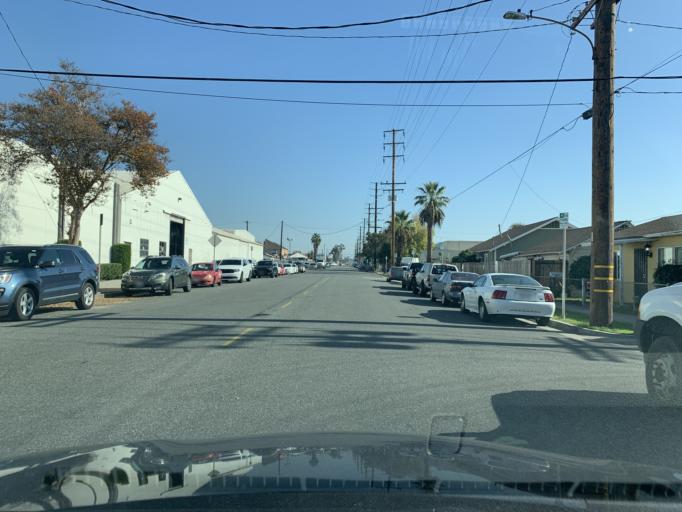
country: US
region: California
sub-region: Los Angeles County
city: Covina
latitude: 34.0916
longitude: -117.8876
